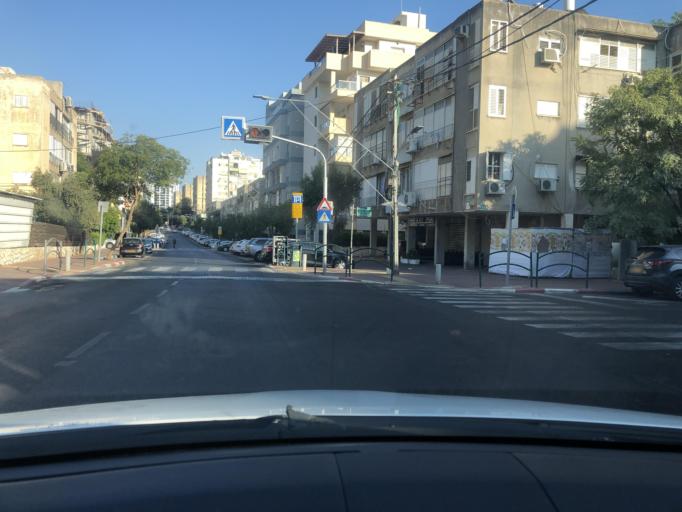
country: IL
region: Tel Aviv
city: Giv`atayim
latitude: 32.0618
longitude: 34.8253
